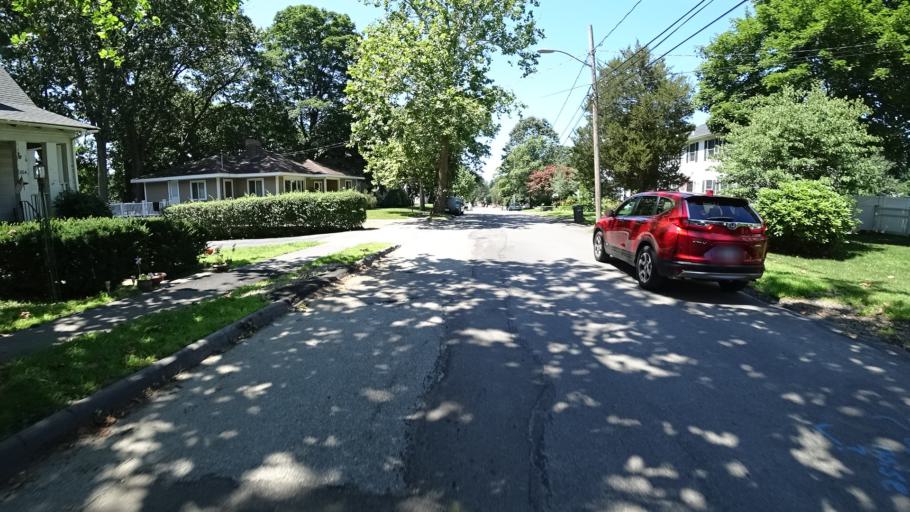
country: US
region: Massachusetts
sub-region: Norfolk County
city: Dedham
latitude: 42.2350
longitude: -71.1604
